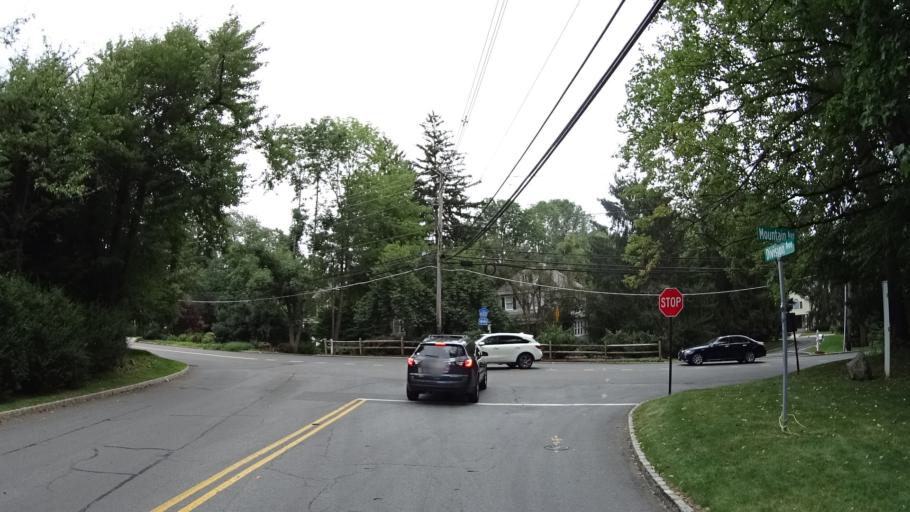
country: US
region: New Jersey
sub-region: Union County
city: New Providence
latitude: 40.6999
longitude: -74.3817
